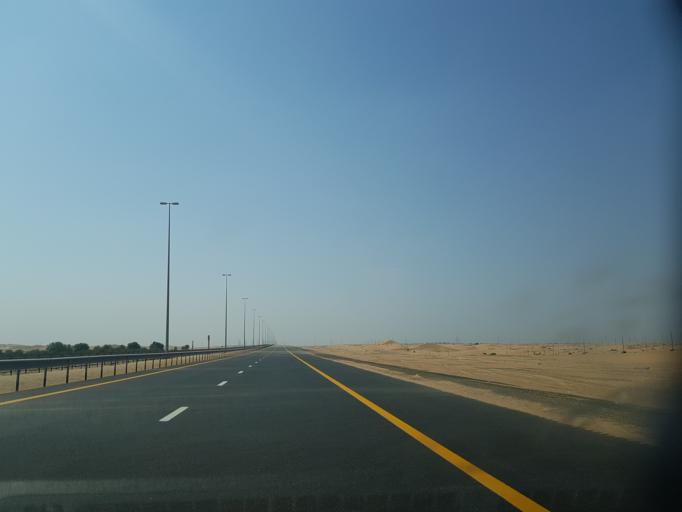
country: AE
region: Ash Shariqah
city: Sharjah
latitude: 25.2755
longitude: 55.6180
